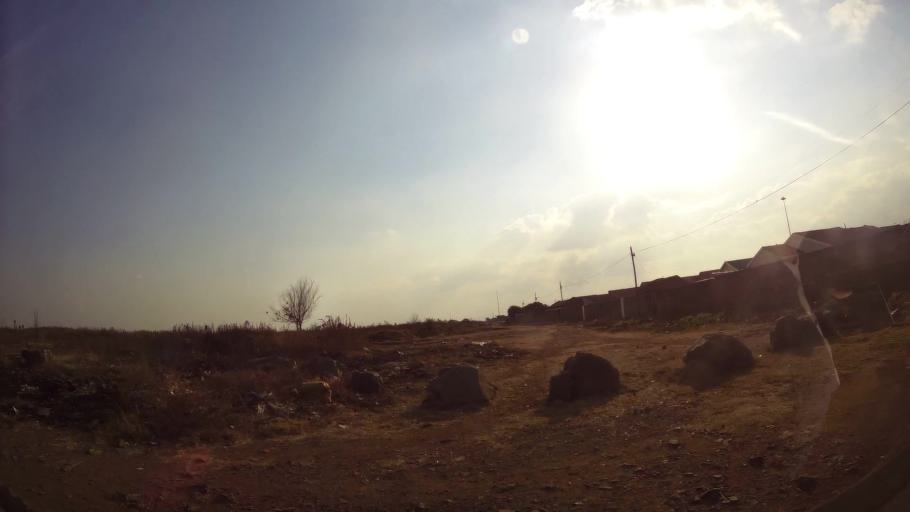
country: ZA
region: Gauteng
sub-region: Ekurhuleni Metropolitan Municipality
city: Germiston
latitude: -26.3683
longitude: 28.2059
